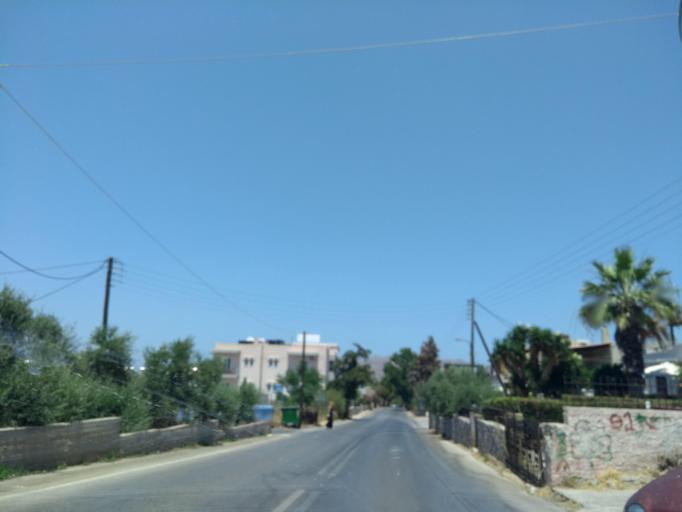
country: GR
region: Crete
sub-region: Nomos Chanias
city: Pithari
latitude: 35.5472
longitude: 24.0828
